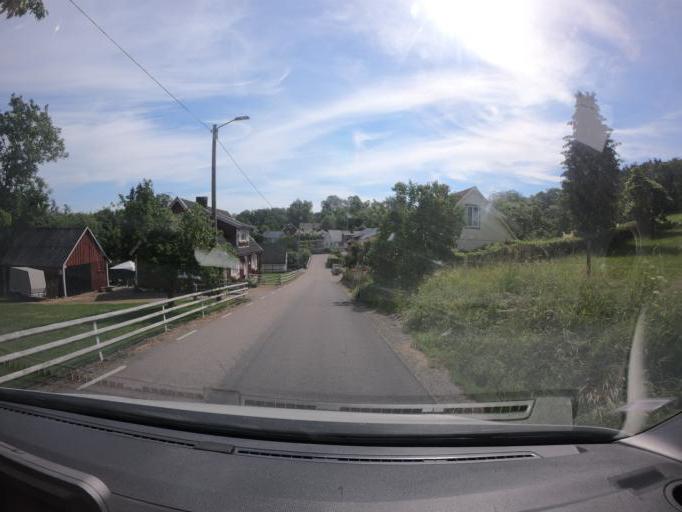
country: SE
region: Skane
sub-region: Bastads Kommun
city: Bastad
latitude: 56.4168
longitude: 12.9442
